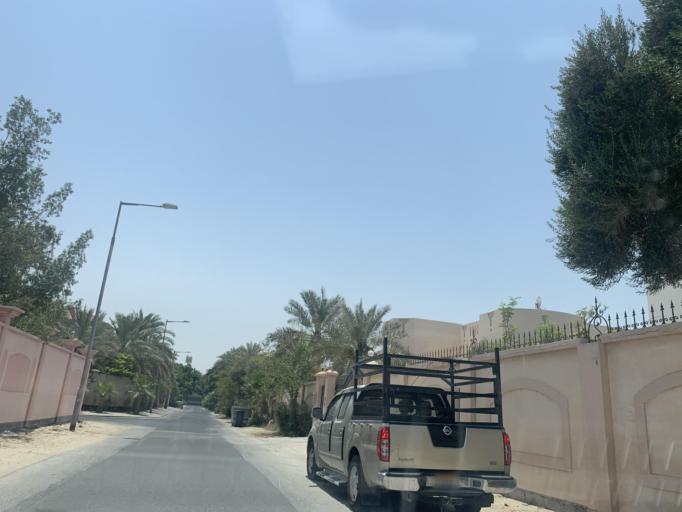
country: BH
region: Manama
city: Jidd Hafs
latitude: 26.2080
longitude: 50.4737
